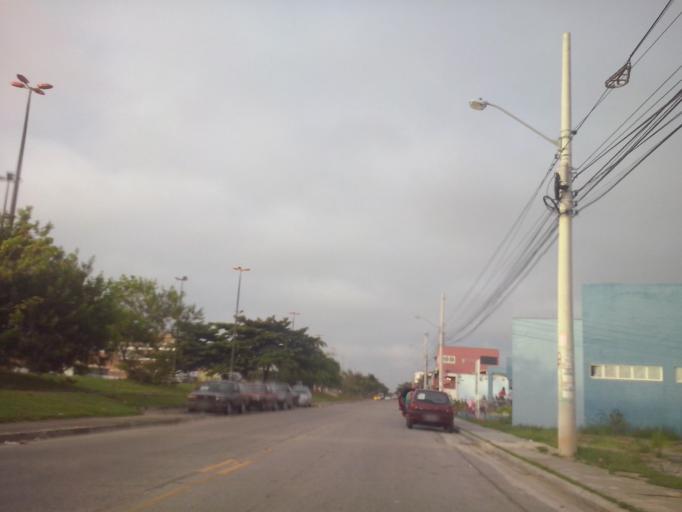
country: BR
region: Rio de Janeiro
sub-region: Rio Das Ostras
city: Rio das Ostras
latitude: -22.5490
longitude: -41.9749
